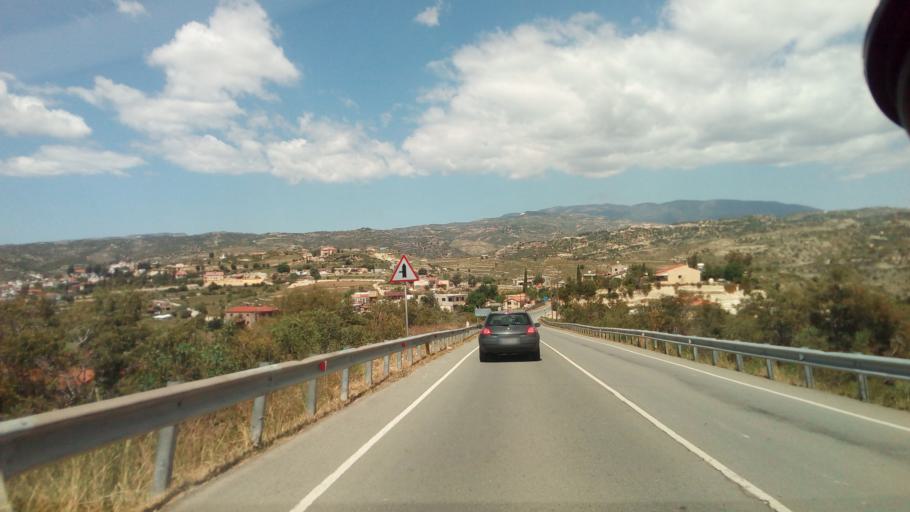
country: CY
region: Limassol
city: Pachna
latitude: 34.7744
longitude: 32.8324
